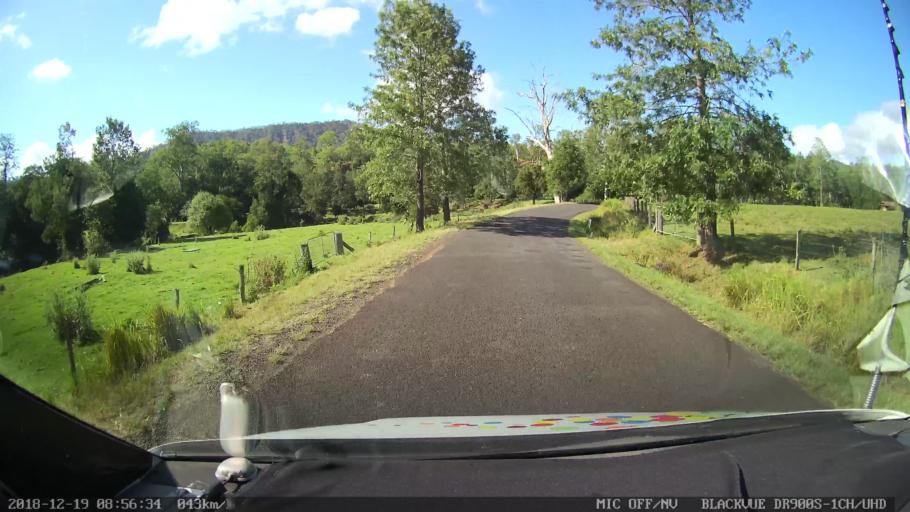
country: AU
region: New South Wales
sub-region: Kyogle
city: Kyogle
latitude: -28.4197
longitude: 152.9763
